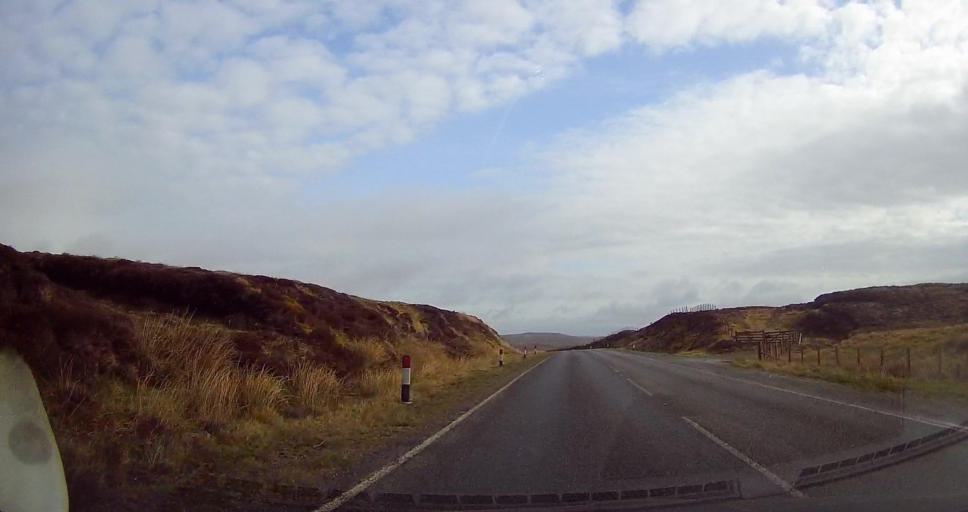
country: GB
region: Scotland
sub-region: Shetland Islands
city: Sandwick
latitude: 60.0873
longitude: -1.2311
